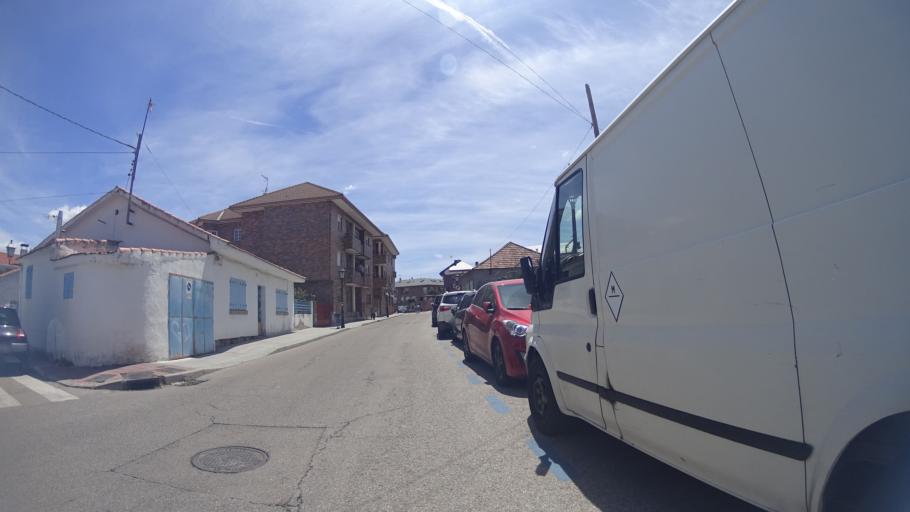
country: ES
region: Madrid
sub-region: Provincia de Madrid
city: Galapagar
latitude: 40.5783
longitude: -4.0080
